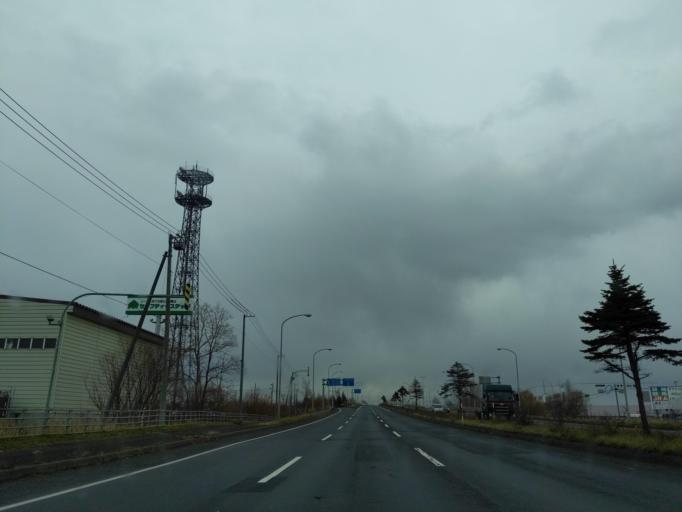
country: JP
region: Hokkaido
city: Ishikari
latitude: 43.1849
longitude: 141.3183
